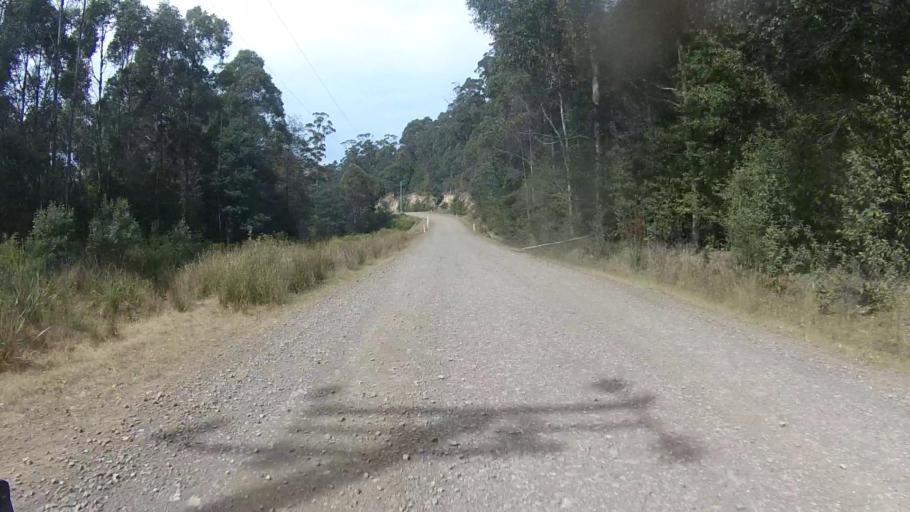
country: AU
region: Tasmania
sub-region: Sorell
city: Sorell
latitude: -42.7700
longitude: 147.8308
